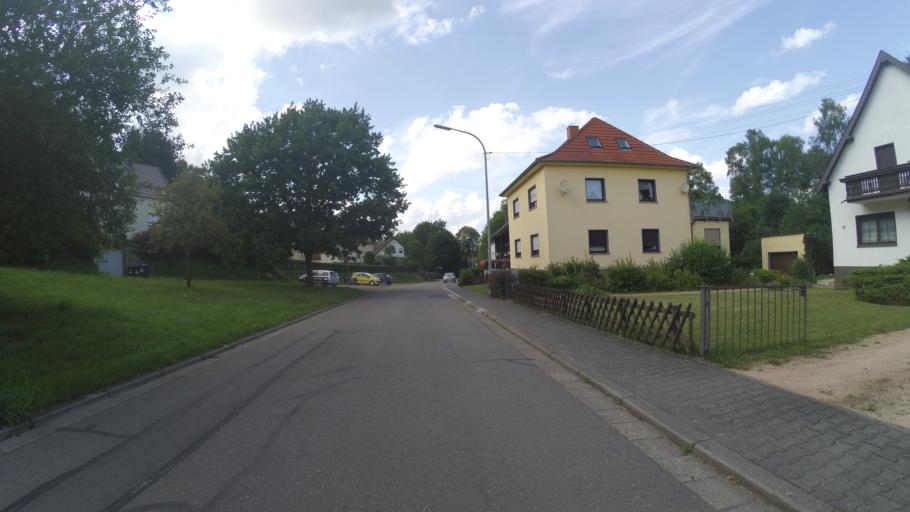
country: DE
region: Saarland
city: Nohfelden
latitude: 49.5794
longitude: 7.1448
